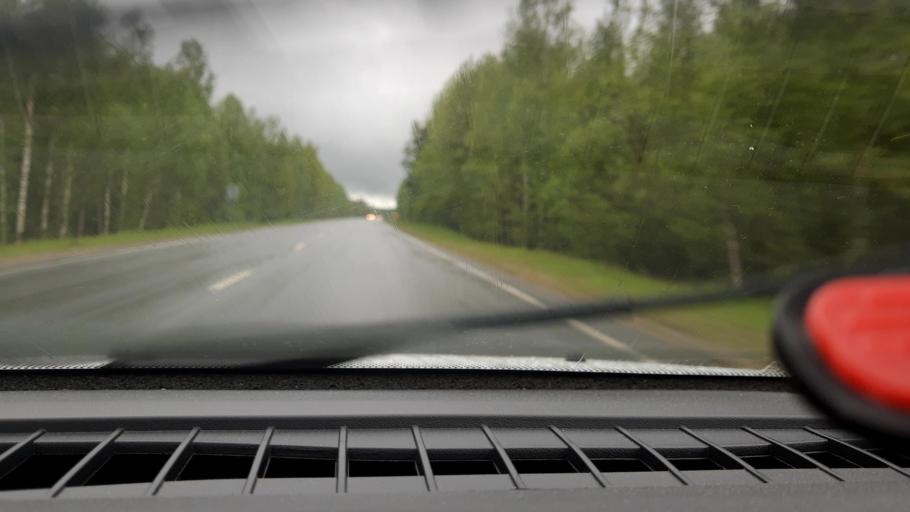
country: RU
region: Nizjnij Novgorod
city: Semenov
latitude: 56.7848
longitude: 44.4409
